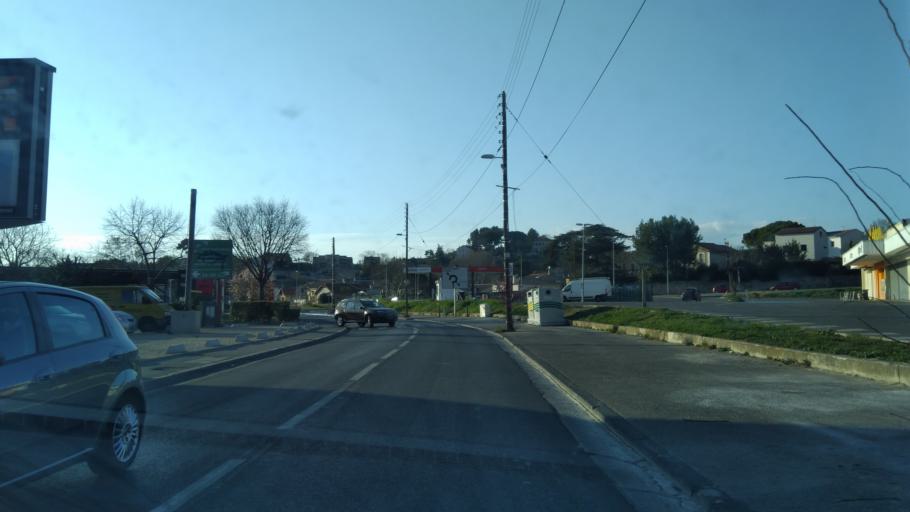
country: FR
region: Provence-Alpes-Cote d'Azur
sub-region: Departement des Bouches-du-Rhone
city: Plan-de-Cuques
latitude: 43.3344
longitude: 5.4548
